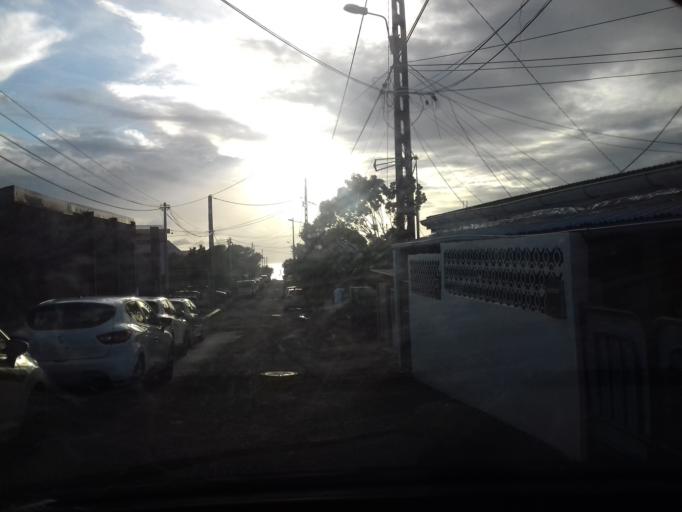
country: MQ
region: Martinique
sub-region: Martinique
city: Fort-de-France
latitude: 14.6168
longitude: -61.0892
